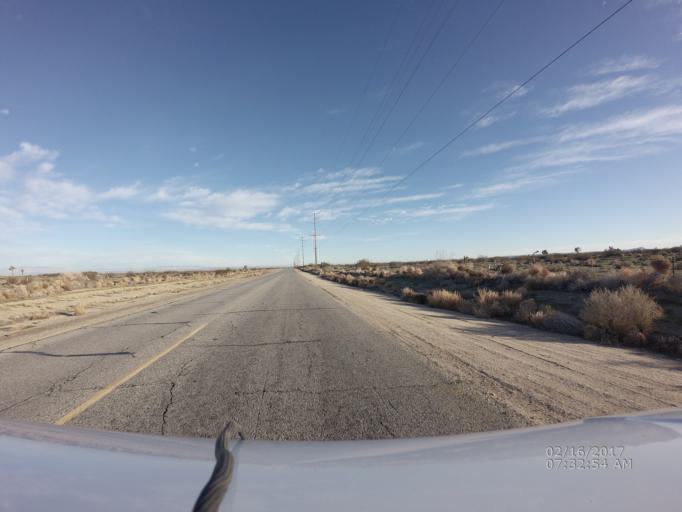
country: US
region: California
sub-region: Los Angeles County
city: Littlerock
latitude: 34.6380
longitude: -117.9697
